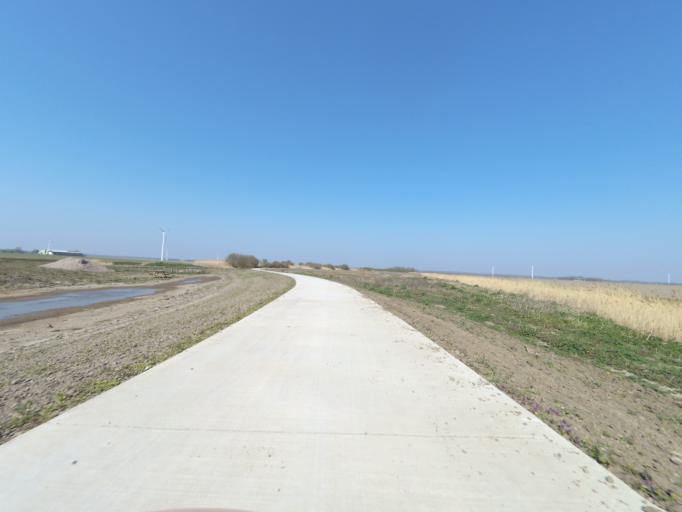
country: NL
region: Utrecht
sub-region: Gemeente Bunschoten
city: Spakenburg
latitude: 52.3771
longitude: 5.3696
